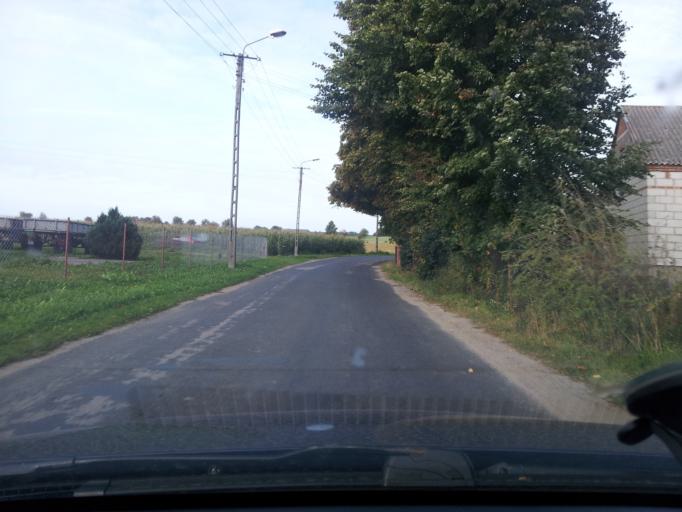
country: PL
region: Kujawsko-Pomorskie
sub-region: Powiat brodnicki
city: Swiedziebnia
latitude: 53.1464
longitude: 19.4922
